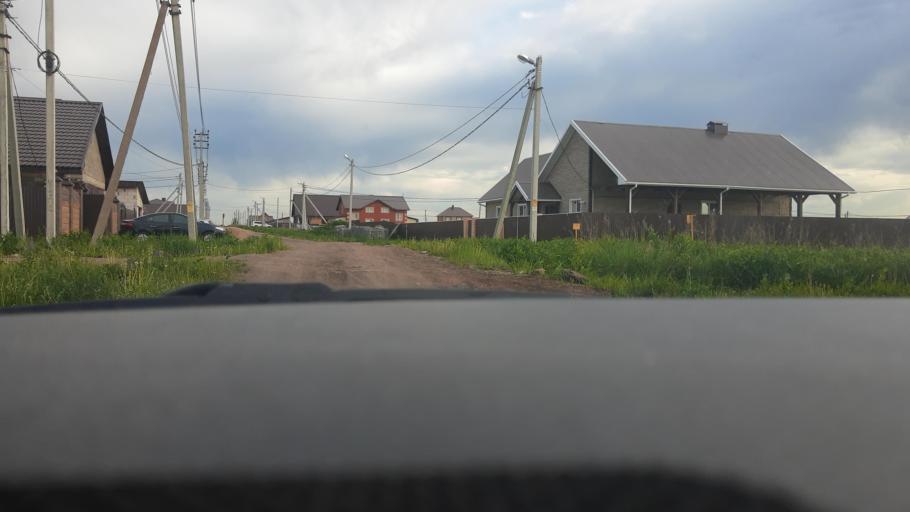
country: RU
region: Bashkortostan
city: Kabakovo
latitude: 54.6064
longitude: 56.1225
